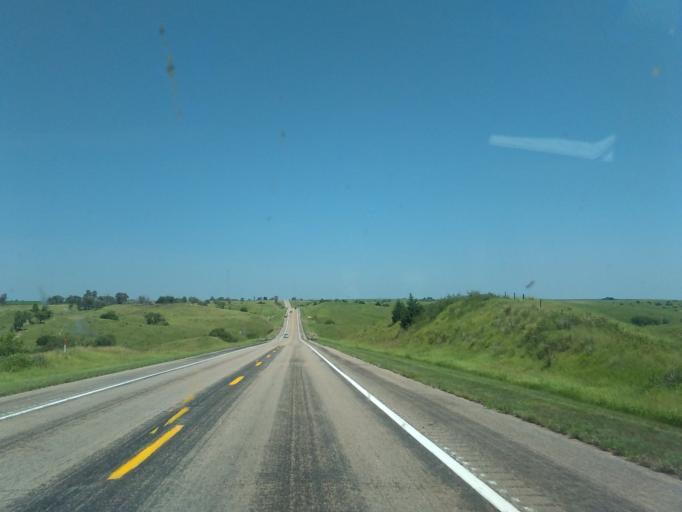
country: US
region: Nebraska
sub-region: Frontier County
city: Stockville
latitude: 40.5824
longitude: -100.6296
